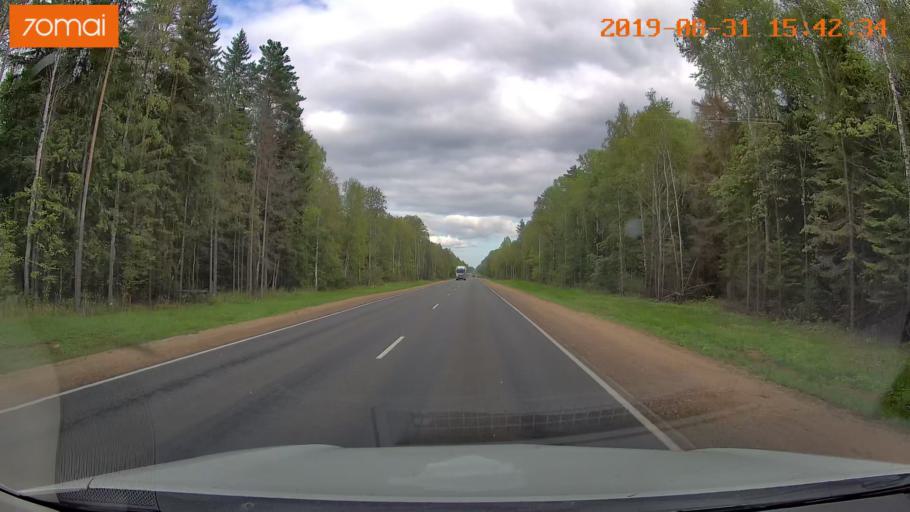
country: RU
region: Kaluga
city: Mosal'sk
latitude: 54.6470
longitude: 34.8892
